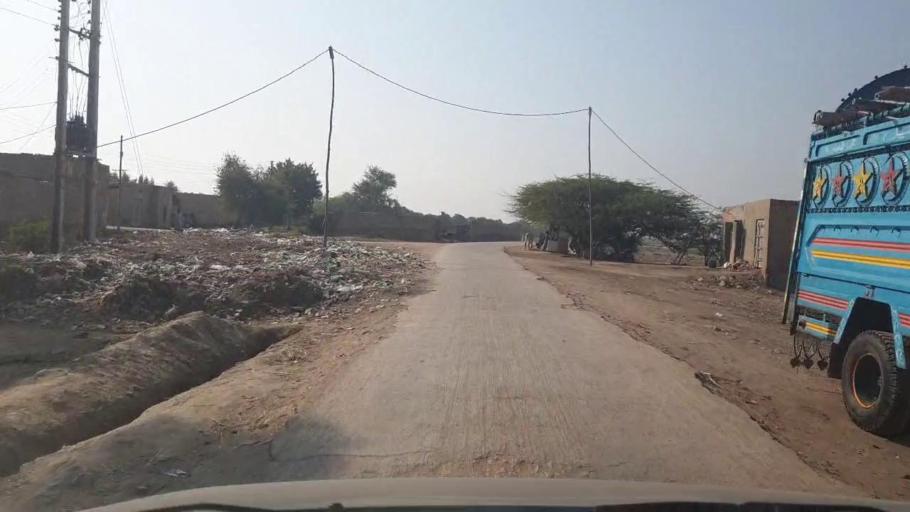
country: PK
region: Sindh
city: Mirwah Gorchani
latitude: 25.3117
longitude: 69.1522
